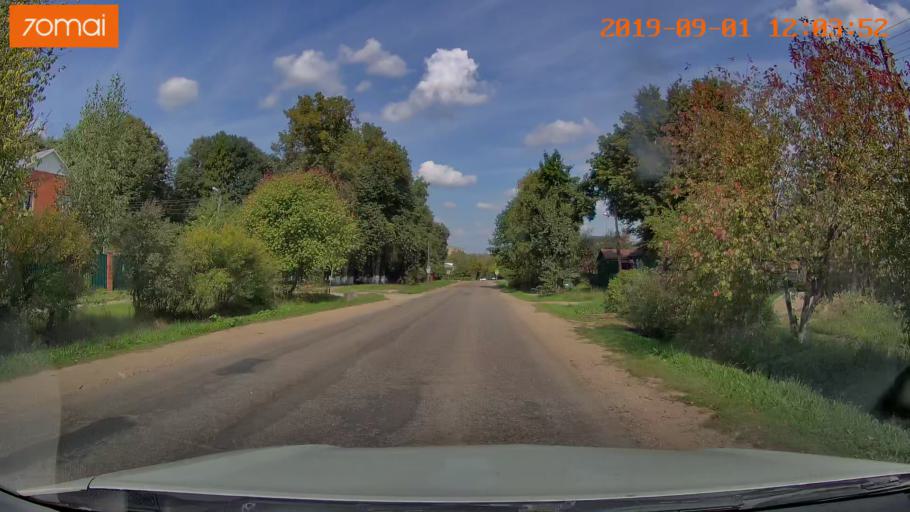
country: RU
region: Kaluga
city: Maloyaroslavets
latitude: 54.9930
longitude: 36.4710
